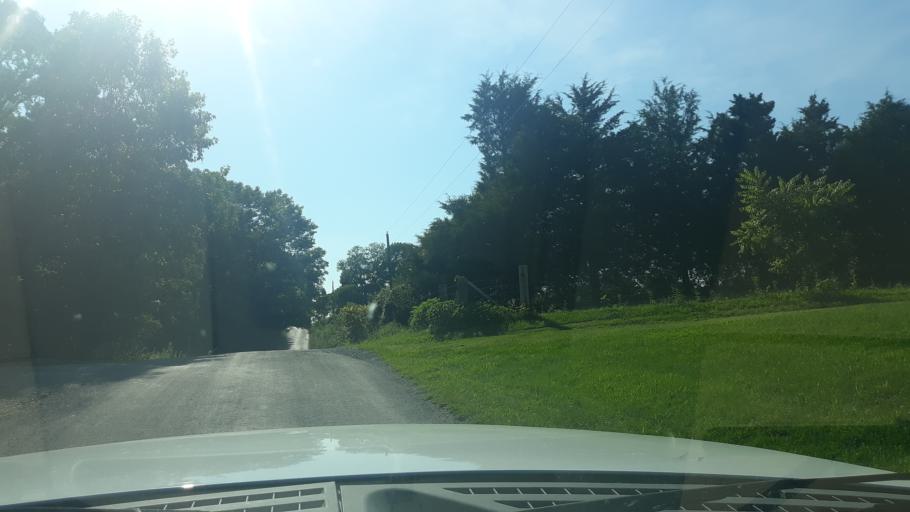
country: US
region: Illinois
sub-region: Saline County
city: Harrisburg
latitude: 37.8524
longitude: -88.5971
